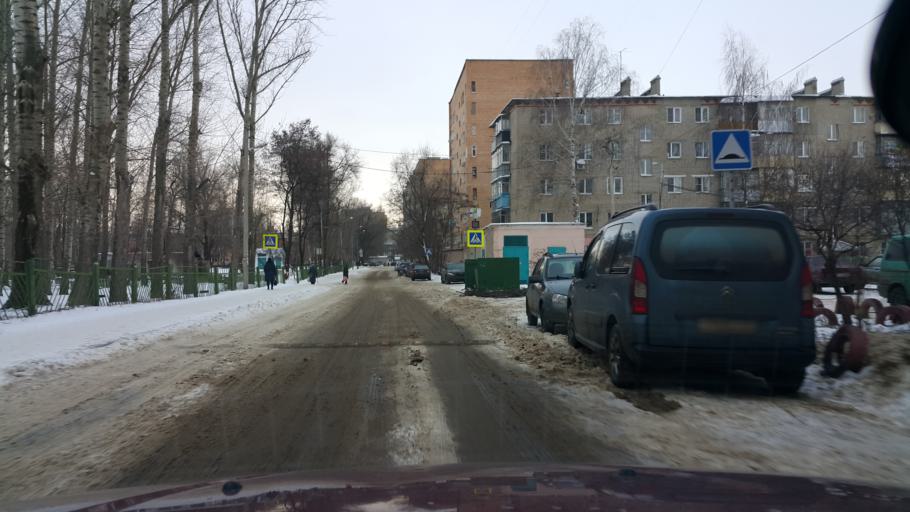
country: RU
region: Tambov
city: Bokino
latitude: 52.6537
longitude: 41.4486
